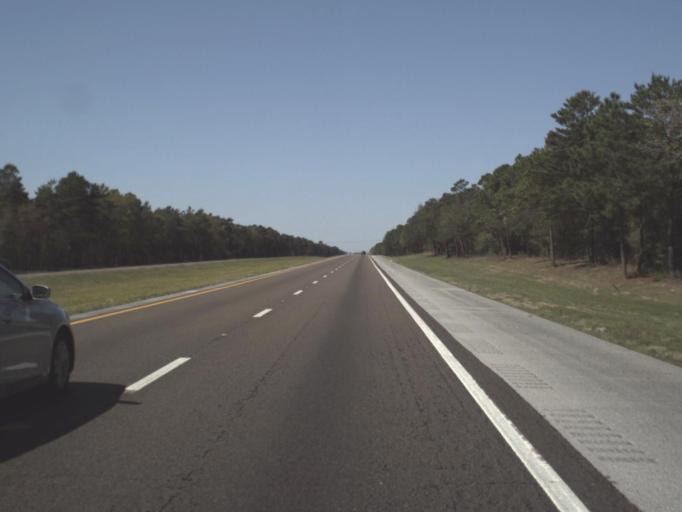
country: US
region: Florida
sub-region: Walton County
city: DeFuniak Springs
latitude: 30.7445
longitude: -86.3060
